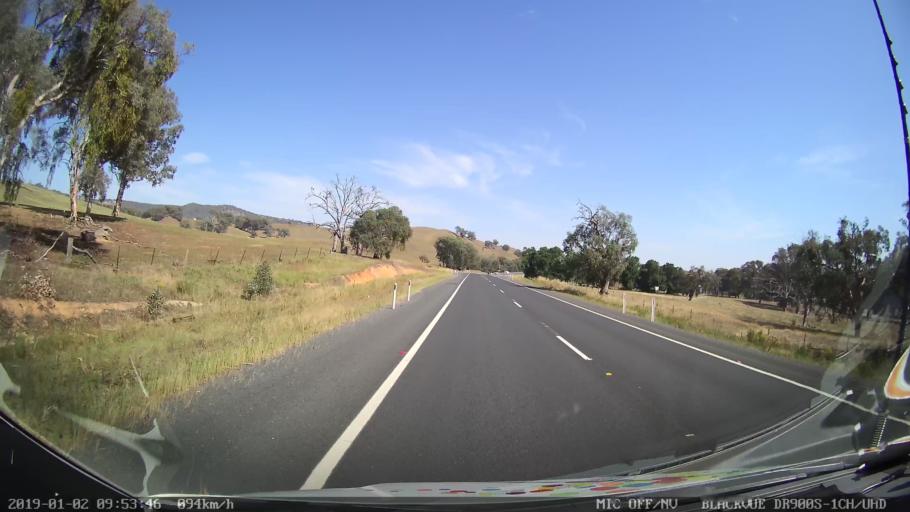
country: AU
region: New South Wales
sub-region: Tumut Shire
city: Tumut
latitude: -35.2440
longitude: 148.2003
